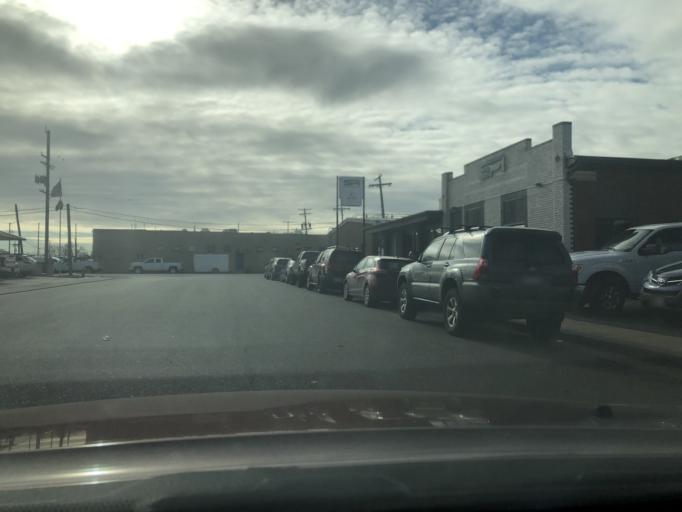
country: US
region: Colorado
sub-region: Denver County
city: Denver
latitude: 39.6936
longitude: -104.9914
